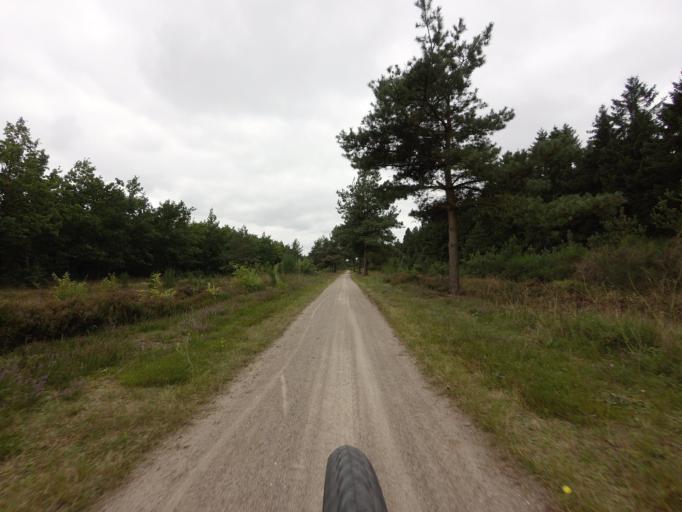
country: DK
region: South Denmark
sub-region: Billund Kommune
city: Grindsted
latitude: 55.7782
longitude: 8.9372
